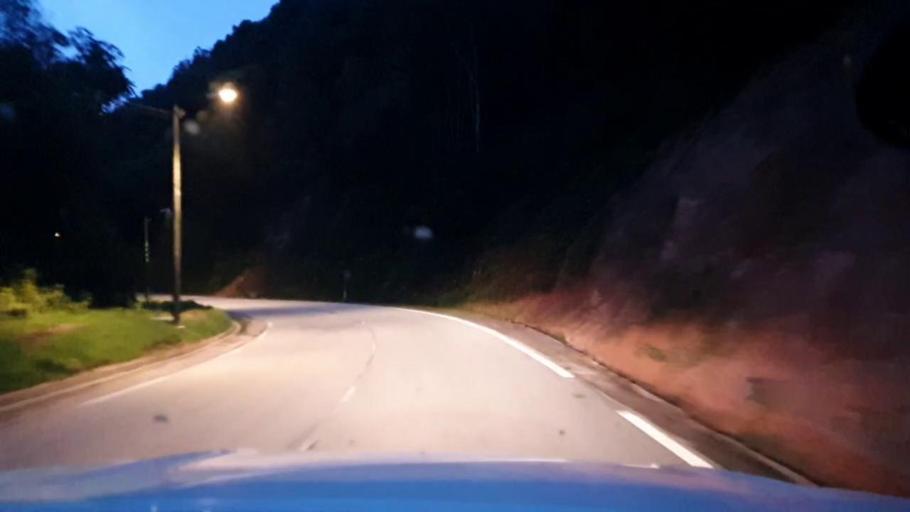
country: RW
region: Southern Province
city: Nzega
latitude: -2.5315
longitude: 29.3911
